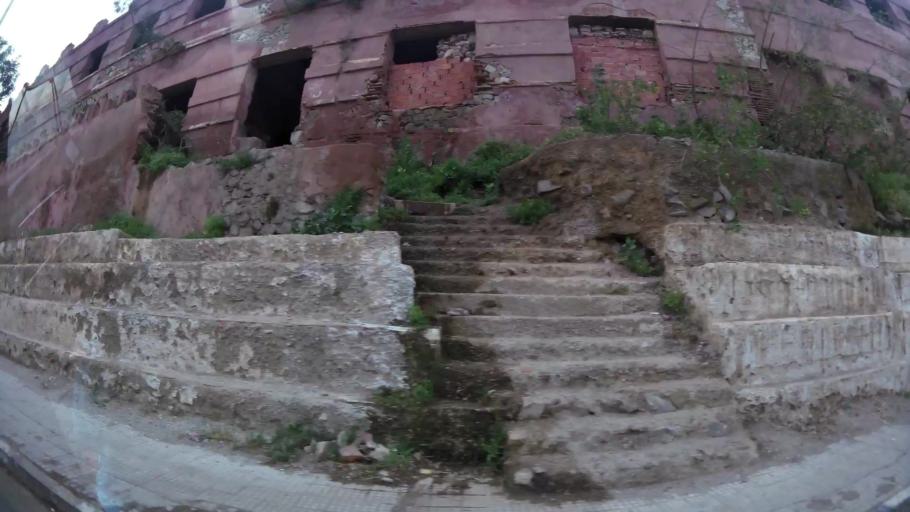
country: MA
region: Oriental
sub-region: Nador
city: Nador
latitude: 35.1877
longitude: -2.9291
